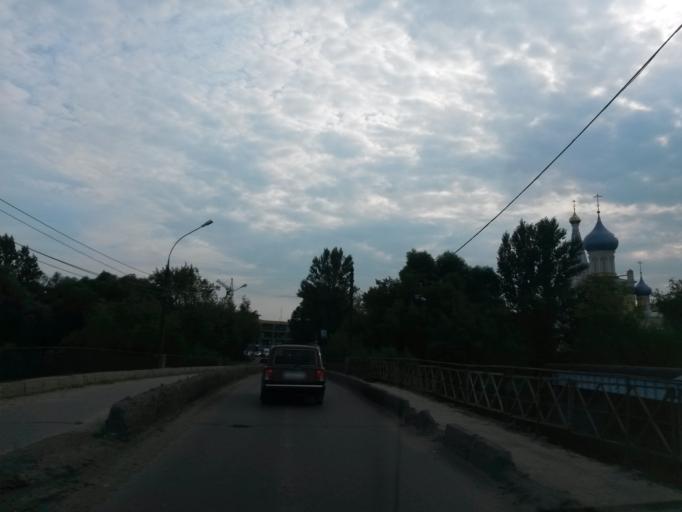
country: RU
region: Jaroslavl
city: Yaroslavl
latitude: 57.6101
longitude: 39.8375
